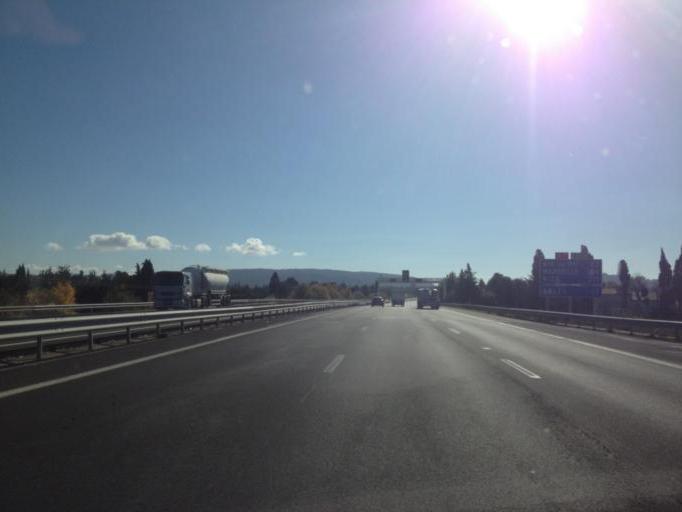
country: FR
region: Provence-Alpes-Cote d'Azur
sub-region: Departement des Bouches-du-Rhone
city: Senas
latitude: 43.7388
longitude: 5.0882
